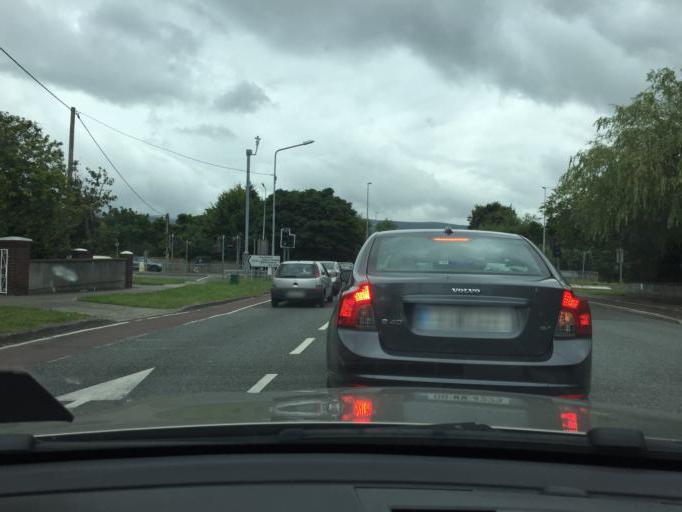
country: IE
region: Leinster
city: Templeogue
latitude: 53.2968
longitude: -6.3093
